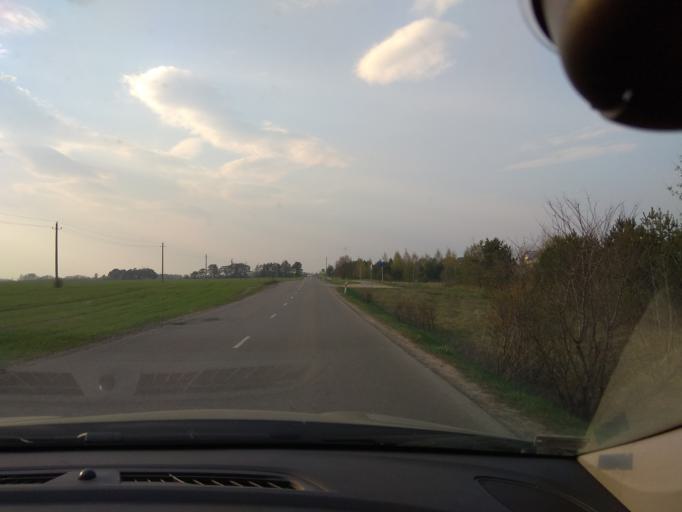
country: LT
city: Grigiskes
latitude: 54.6160
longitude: 25.1177
